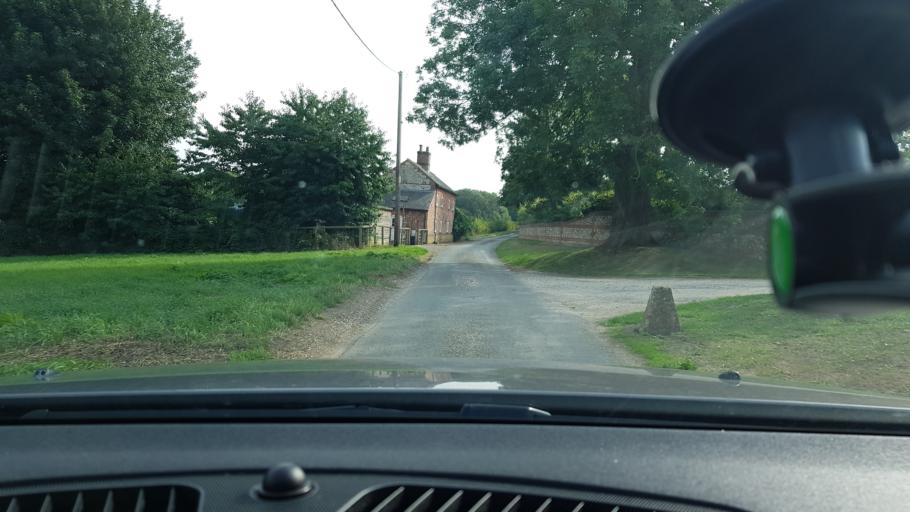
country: GB
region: England
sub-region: Wiltshire
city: Chilton Foliat
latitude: 51.4557
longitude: -1.5648
